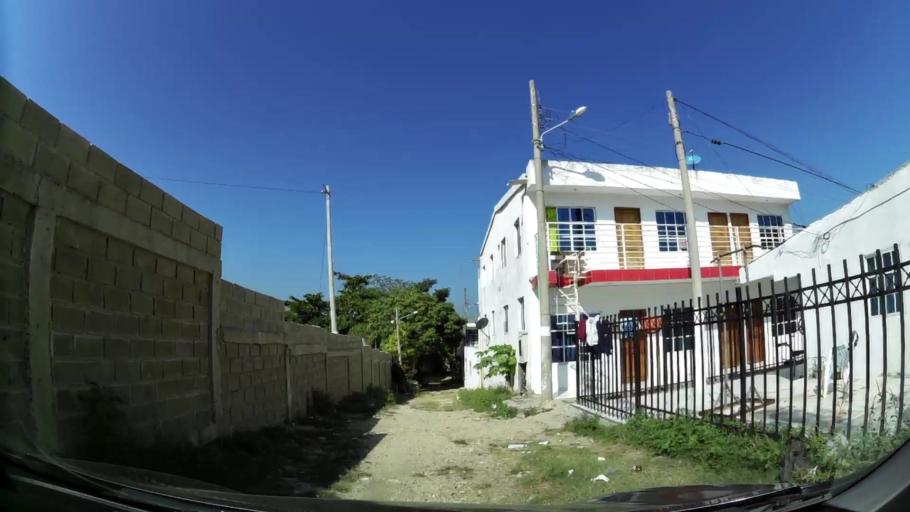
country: CO
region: Bolivar
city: Cartagena
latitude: 10.3689
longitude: -75.5046
